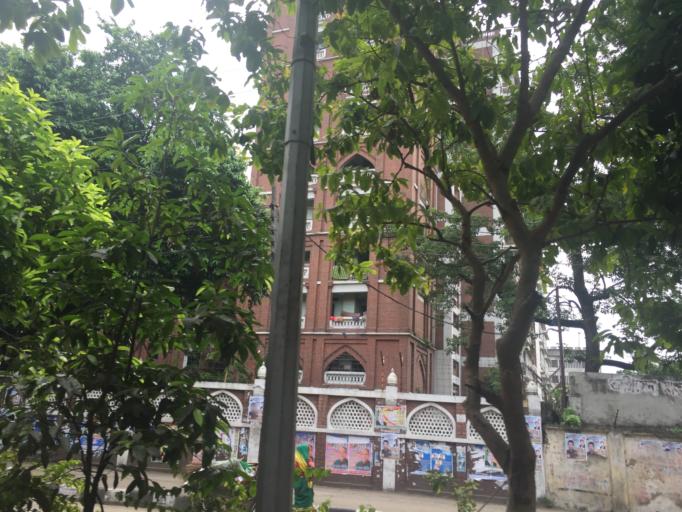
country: BD
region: Dhaka
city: Paltan
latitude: 23.7257
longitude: 90.4046
